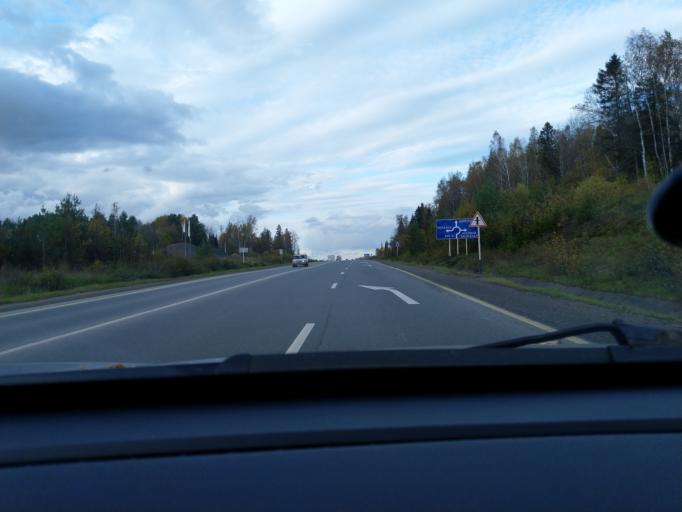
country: RU
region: Perm
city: Polazna
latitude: 58.2904
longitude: 56.4786
